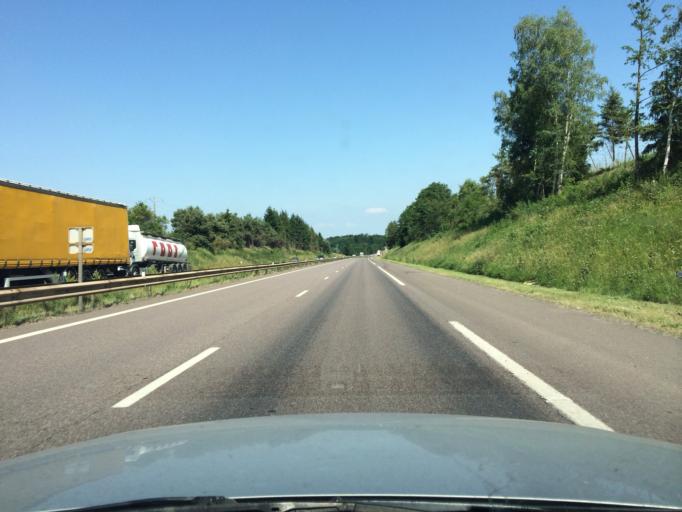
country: FR
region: Alsace
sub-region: Departement du Bas-Rhin
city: Schwindratzheim
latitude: 48.7704
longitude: 7.6147
